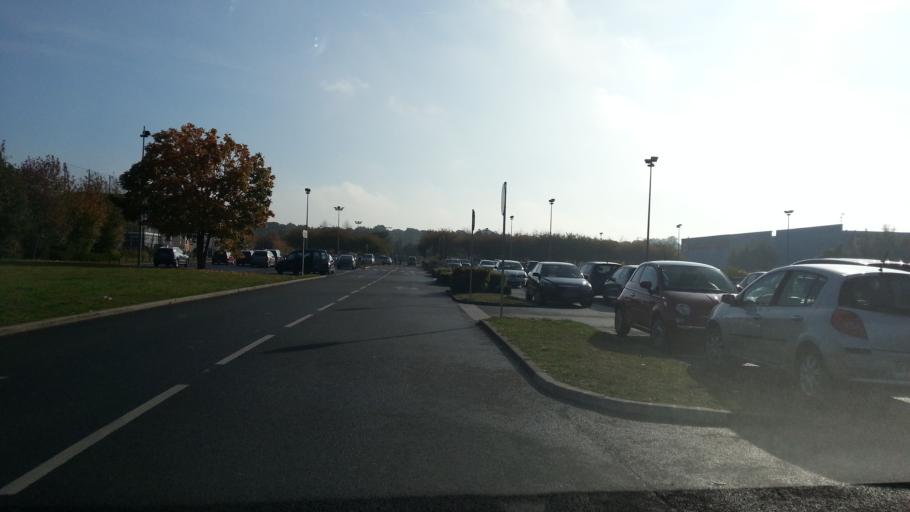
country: FR
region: Picardie
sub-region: Departement de l'Oise
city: Saint-Maximin
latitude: 49.2381
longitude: 2.4660
